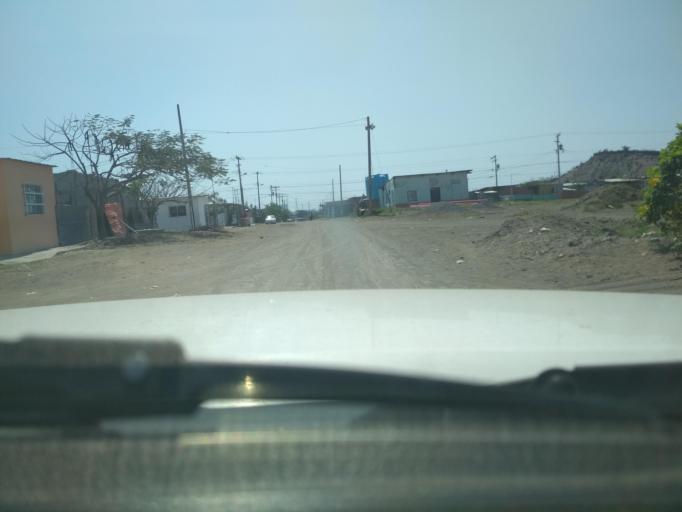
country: MX
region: Veracruz
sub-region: Veracruz
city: Lomas de Rio Medio Cuatro
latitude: 19.1926
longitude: -96.1967
